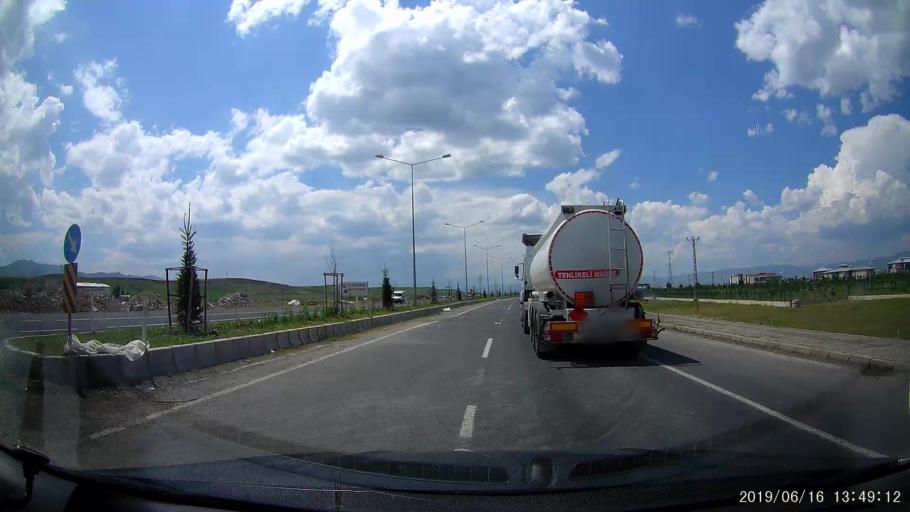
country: TR
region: Agri
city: Agri
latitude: 39.7155
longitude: 42.9943
